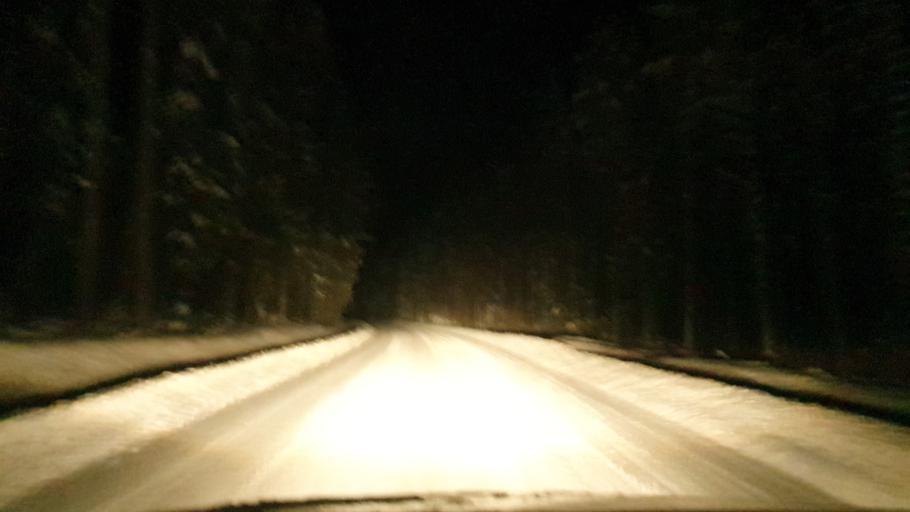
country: EE
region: Vorumaa
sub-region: Antsla vald
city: Vana-Antsla
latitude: 57.9680
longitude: 26.7082
